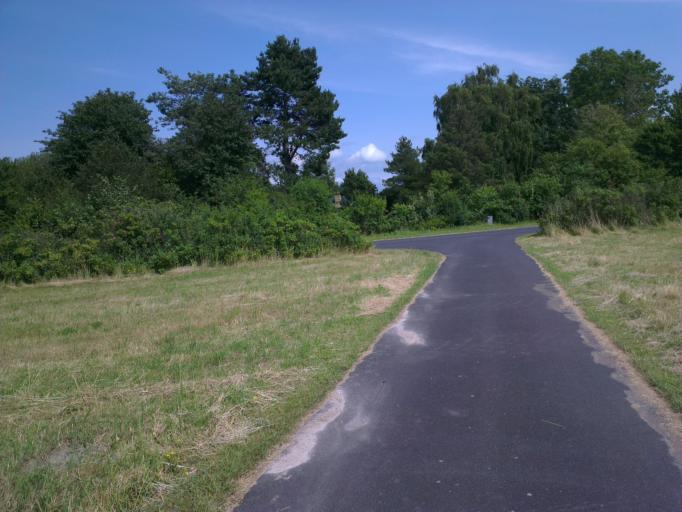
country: DK
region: Capital Region
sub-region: Halsnaes Kommune
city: Hundested
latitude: 55.9341
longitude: 11.9138
